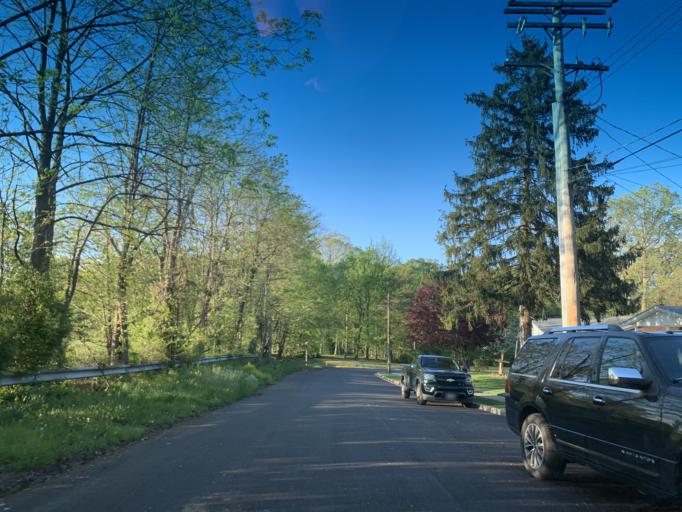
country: US
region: Maryland
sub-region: Harford County
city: Aberdeen
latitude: 39.5150
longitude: -76.1688
